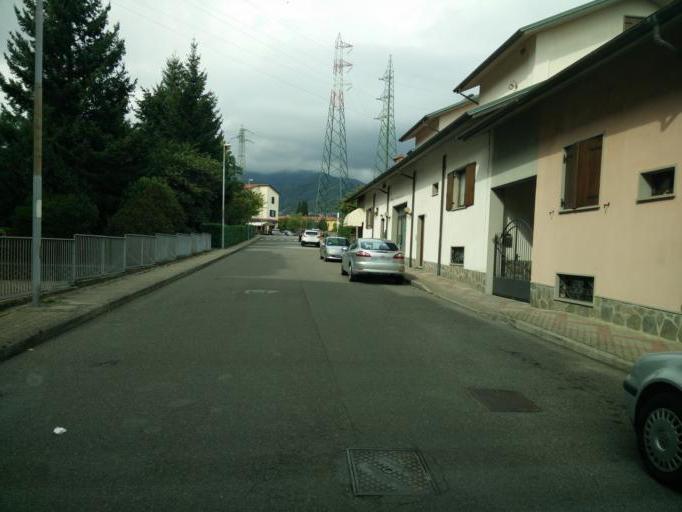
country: IT
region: Tuscany
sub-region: Provincia di Massa-Carrara
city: Pontremoli
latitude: 44.3780
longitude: 9.8759
